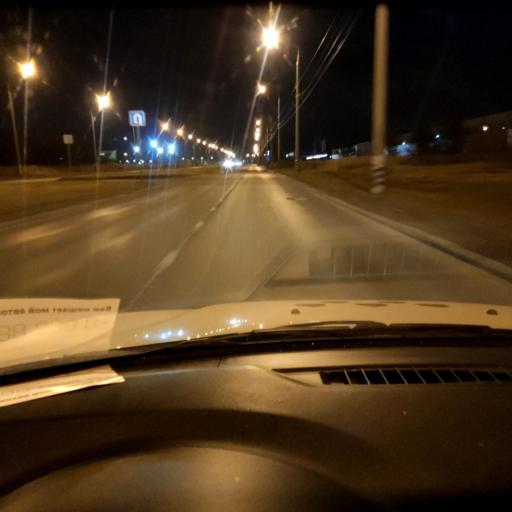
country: RU
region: Samara
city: Tol'yatti
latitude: 53.5572
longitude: 49.3346
